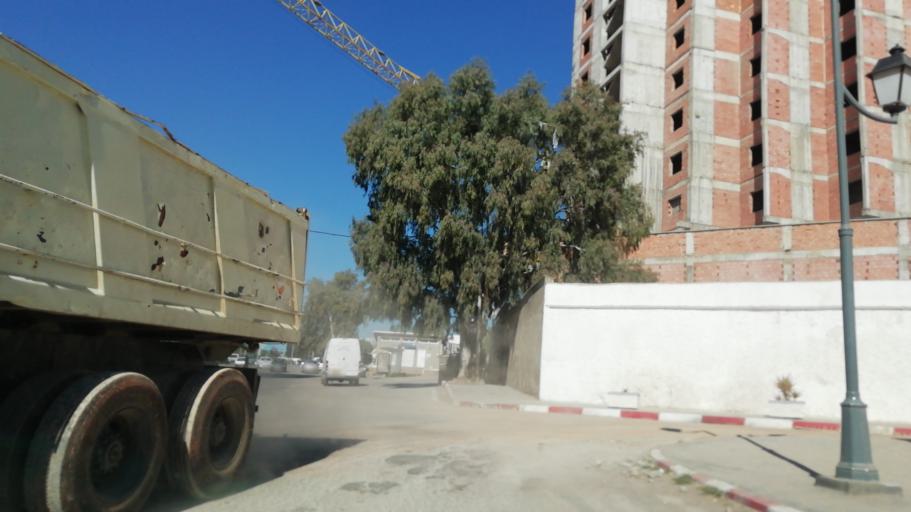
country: DZ
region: Oran
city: Oran
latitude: 35.6957
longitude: -0.6118
